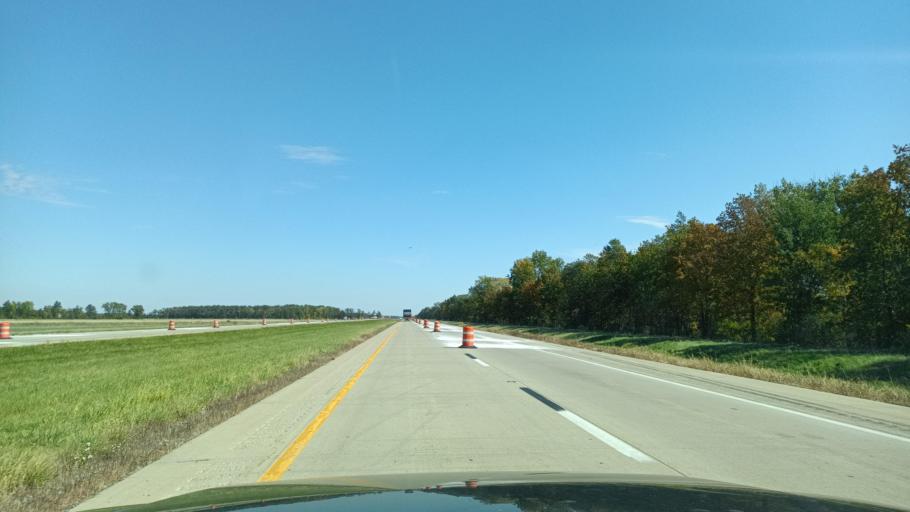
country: US
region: Ohio
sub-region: Paulding County
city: Paulding
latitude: 41.2436
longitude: -84.5059
